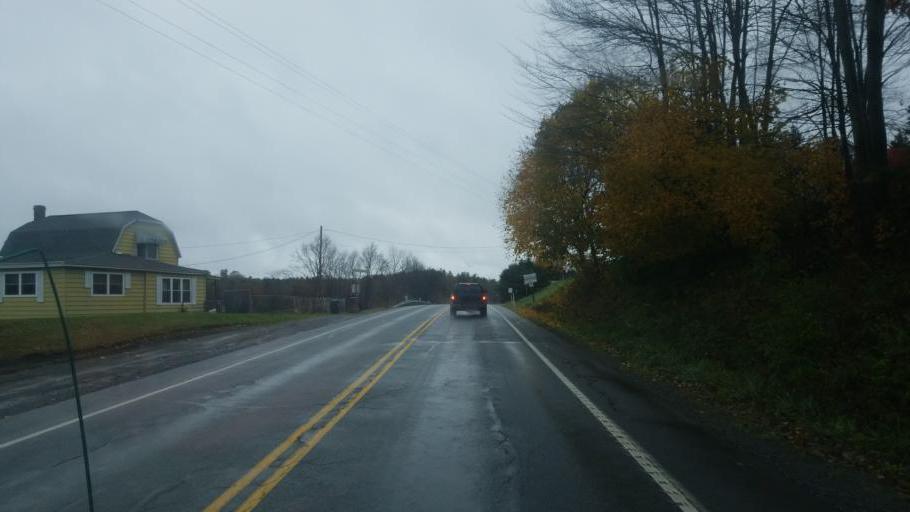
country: US
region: Pennsylvania
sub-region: Clearfield County
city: Shiloh
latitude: 41.1037
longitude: -78.2368
